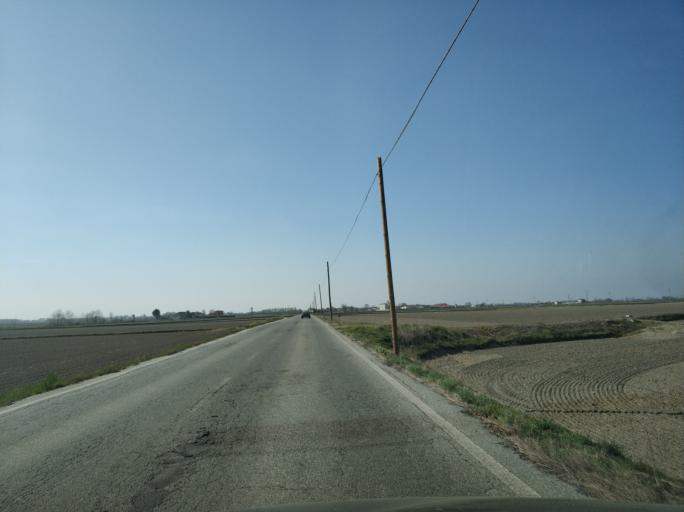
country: IT
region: Piedmont
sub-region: Provincia di Novara
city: Vinzaglio
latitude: 45.3169
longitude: 8.4918
